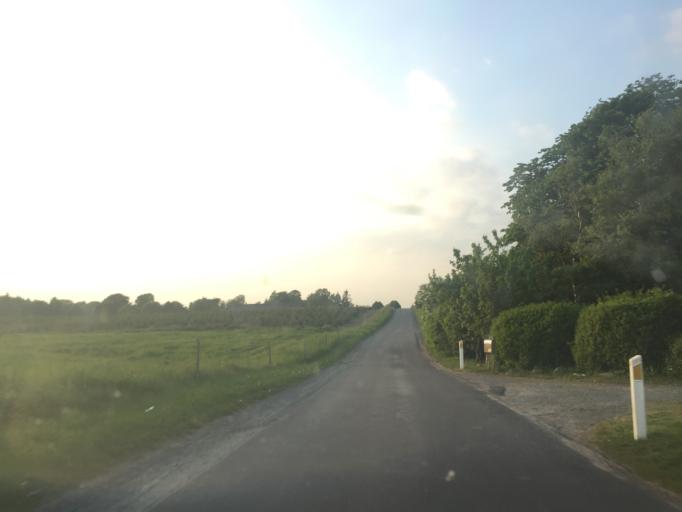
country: DK
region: South Denmark
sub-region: Odense Kommune
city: Bellinge
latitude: 55.3780
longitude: 10.3104
